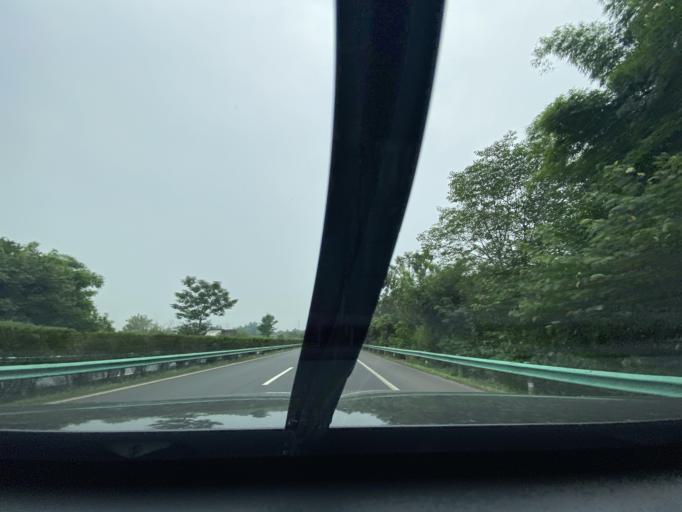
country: CN
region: Sichuan
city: Longquan
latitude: 30.3252
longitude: 104.1207
